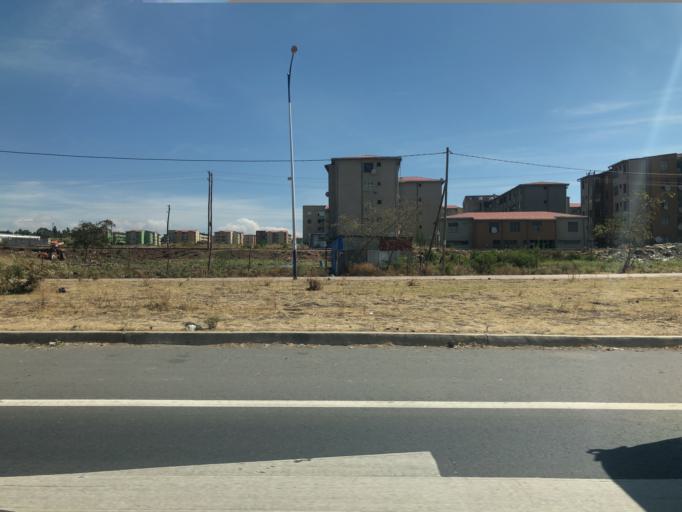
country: ET
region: Adis Abeba
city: Addis Ababa
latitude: 8.8660
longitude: 38.8214
